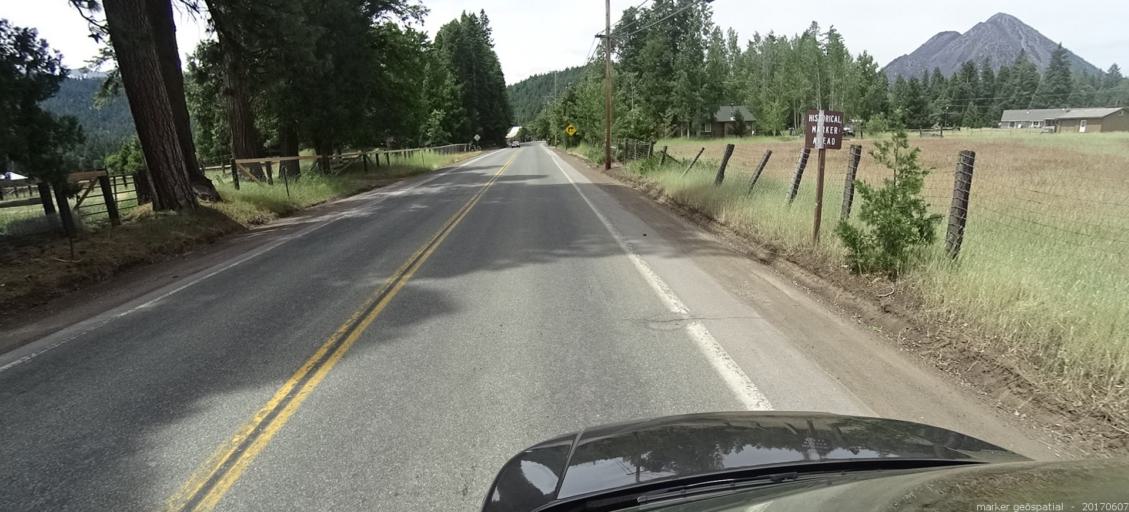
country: US
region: California
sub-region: Siskiyou County
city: Mount Shasta
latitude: 41.3192
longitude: -122.3426
